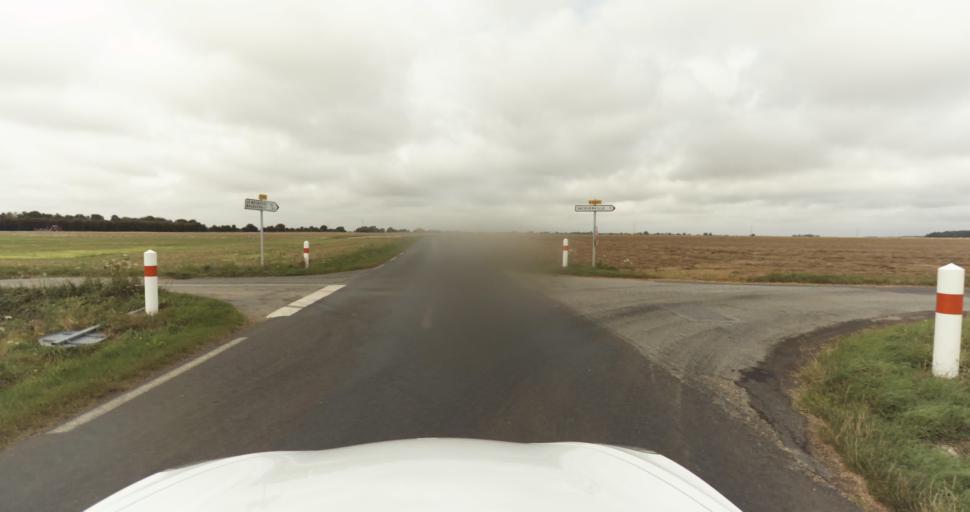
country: FR
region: Haute-Normandie
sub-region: Departement de l'Eure
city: Claville
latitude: 49.0761
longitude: 1.0621
